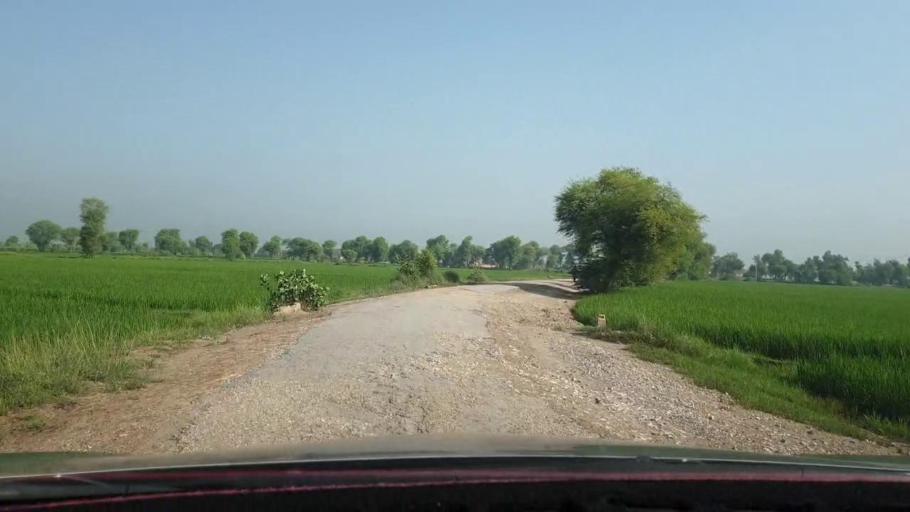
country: PK
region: Sindh
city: Nasirabad
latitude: 27.4465
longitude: 67.9189
